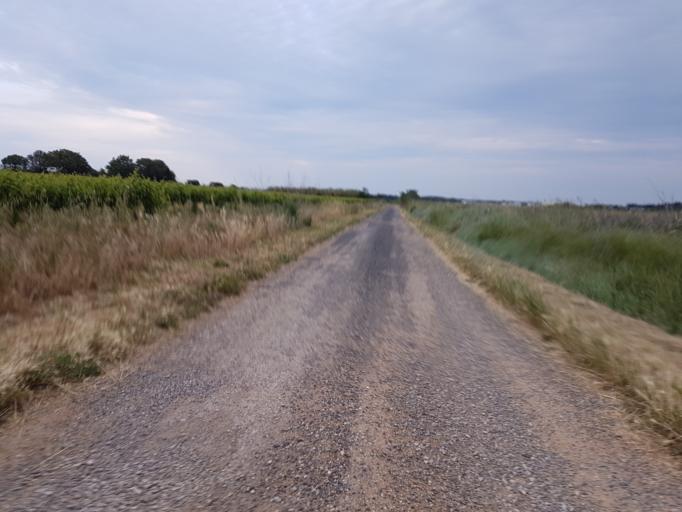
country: FR
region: Languedoc-Roussillon
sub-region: Departement de l'Herault
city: Portiragnes
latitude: 43.3175
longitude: 3.3286
